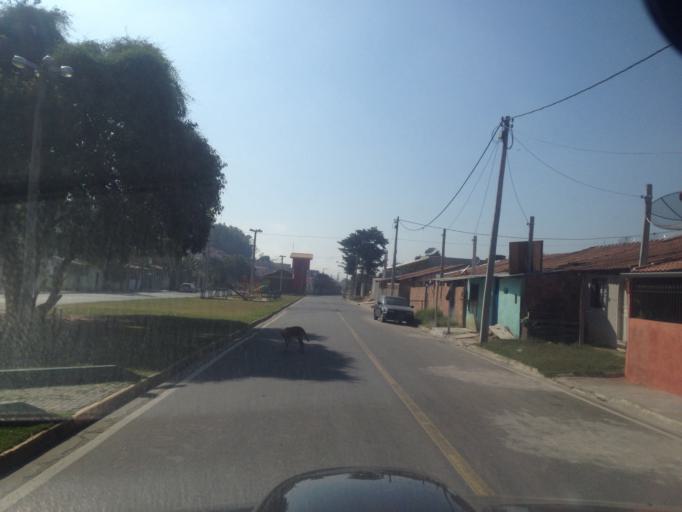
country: BR
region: Rio de Janeiro
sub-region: Porto Real
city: Porto Real
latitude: -22.4402
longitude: -44.3229
